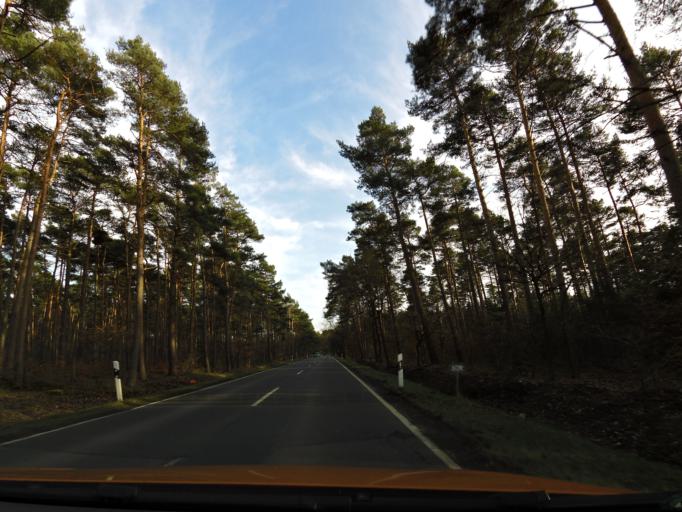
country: DE
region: Lower Saxony
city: Lindwedel
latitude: 52.6167
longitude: 9.7067
